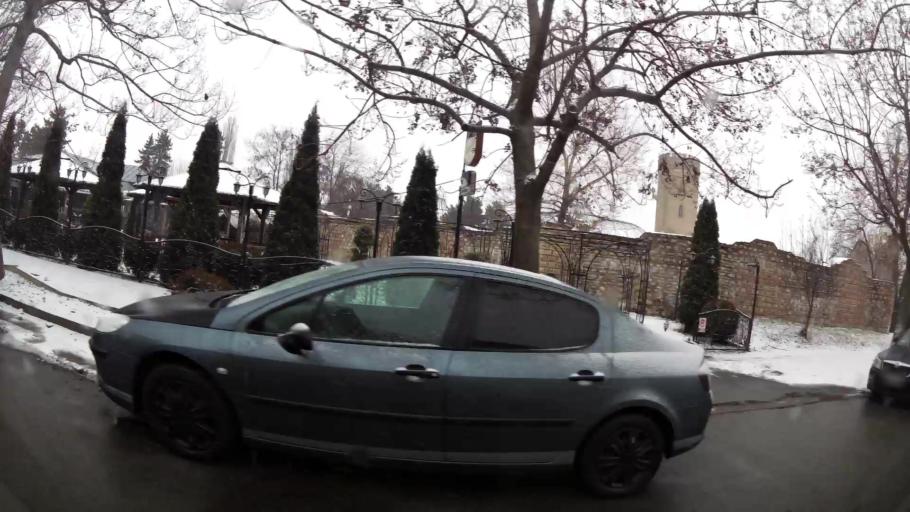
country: RO
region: Dambovita
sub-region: Municipiul Targoviste
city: Targoviste
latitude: 44.9323
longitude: 25.4570
